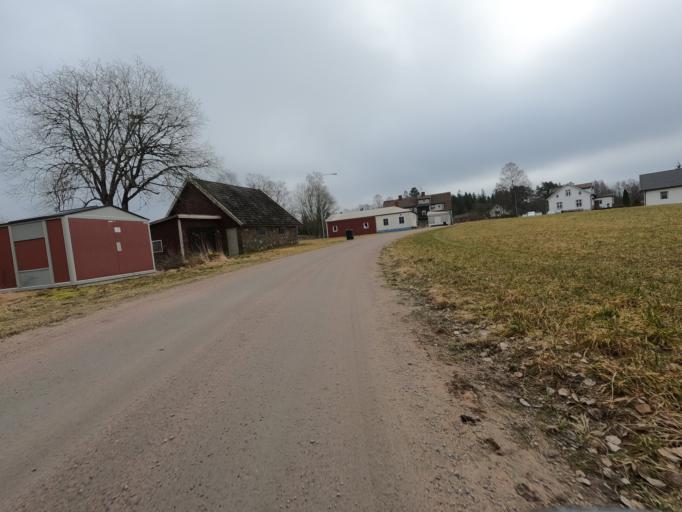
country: SE
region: Kronoberg
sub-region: Markaryds Kommun
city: Stromsnasbruk
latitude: 56.7875
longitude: 13.5629
